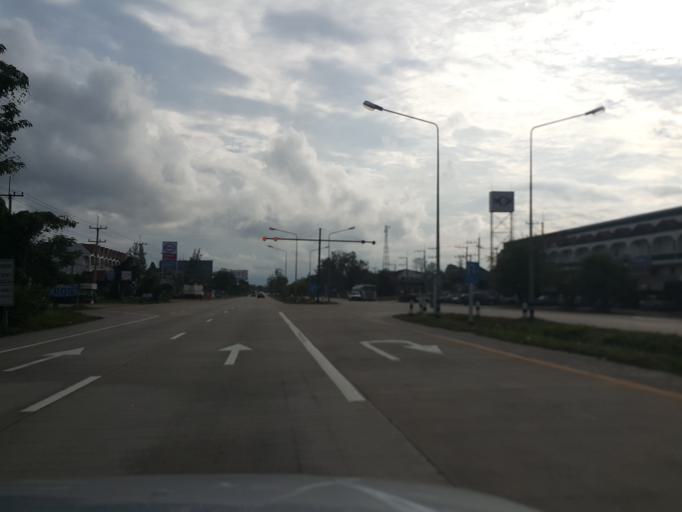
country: TH
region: Lampang
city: Ko Kha
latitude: 18.2203
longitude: 99.4250
